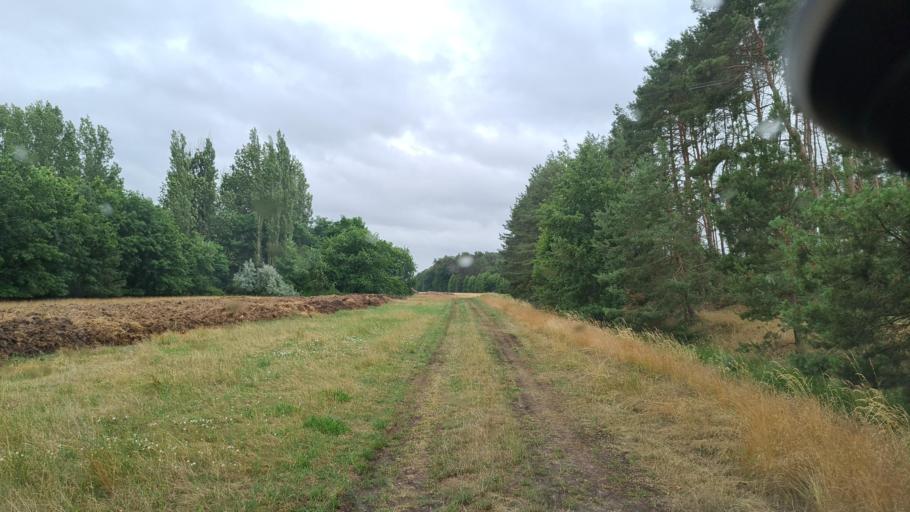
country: DE
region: Saxony-Anhalt
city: Holzdorf
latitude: 51.7893
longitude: 13.1978
